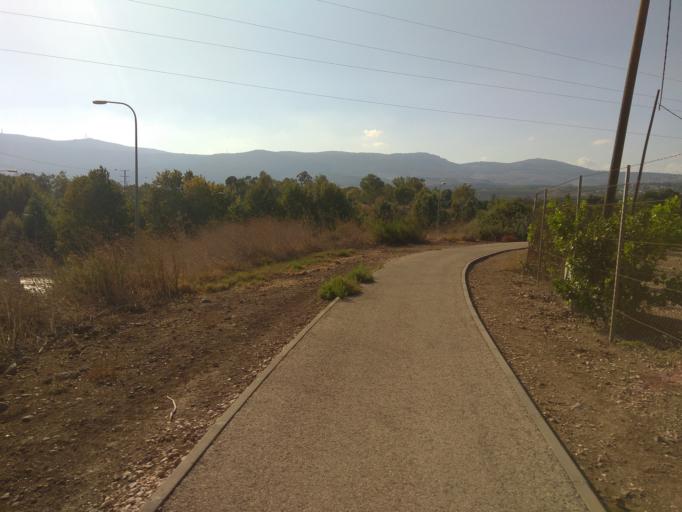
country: IL
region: Northern District
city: Qiryat Shemona
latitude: 33.2254
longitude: 35.6229
